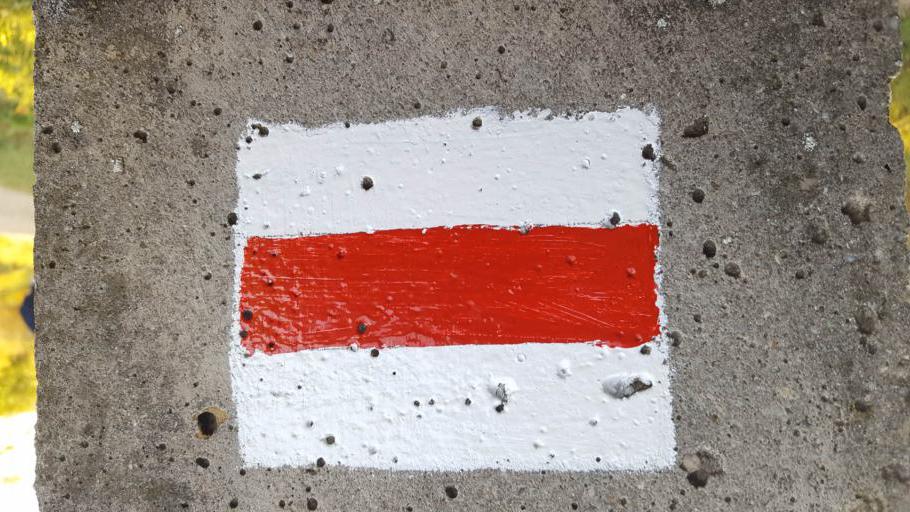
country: HU
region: Somogy
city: Karad
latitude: 46.5858
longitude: 17.9583
